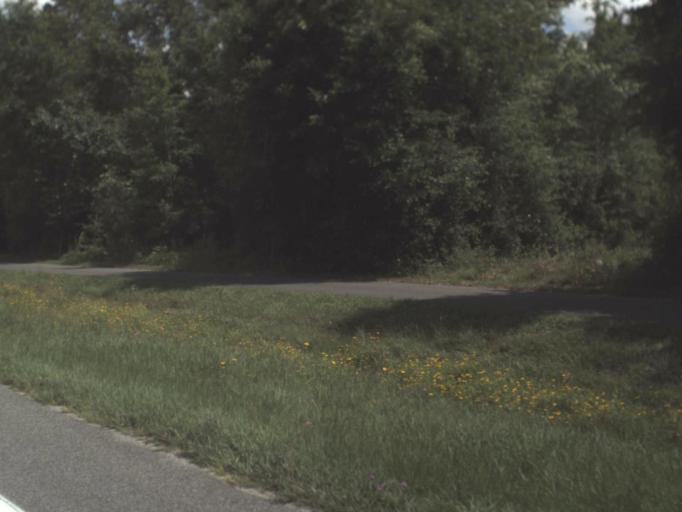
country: US
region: Florida
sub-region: Alachua County
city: High Springs
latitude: 29.9384
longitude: -82.7365
